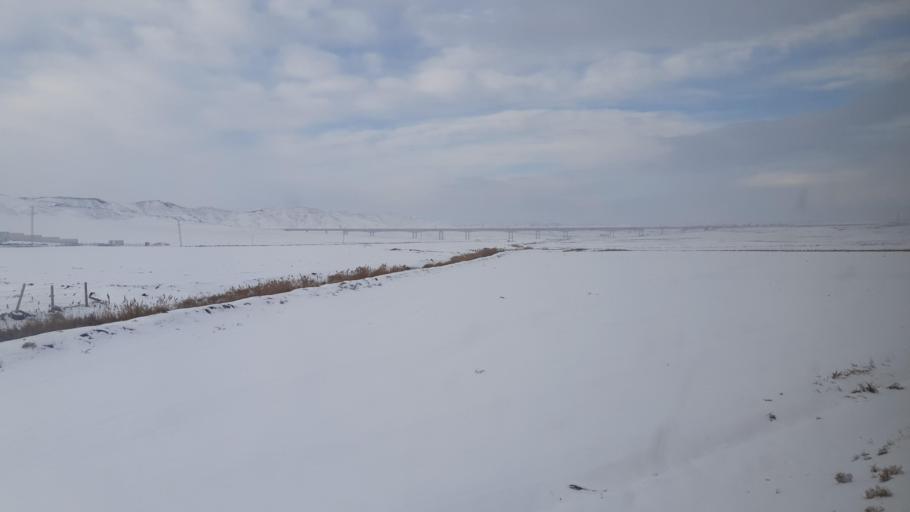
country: TR
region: Kirikkale
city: Delice
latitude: 39.8924
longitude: 33.9925
